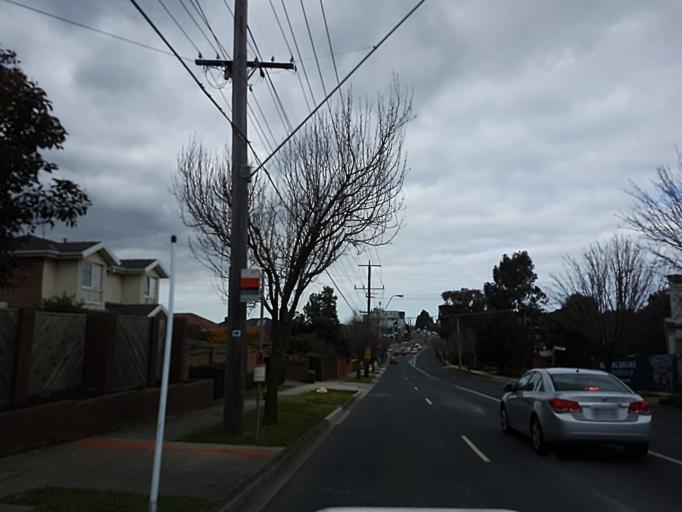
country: AU
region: Victoria
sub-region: Whitehorse
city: Box Hill
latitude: -37.8171
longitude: 145.1392
